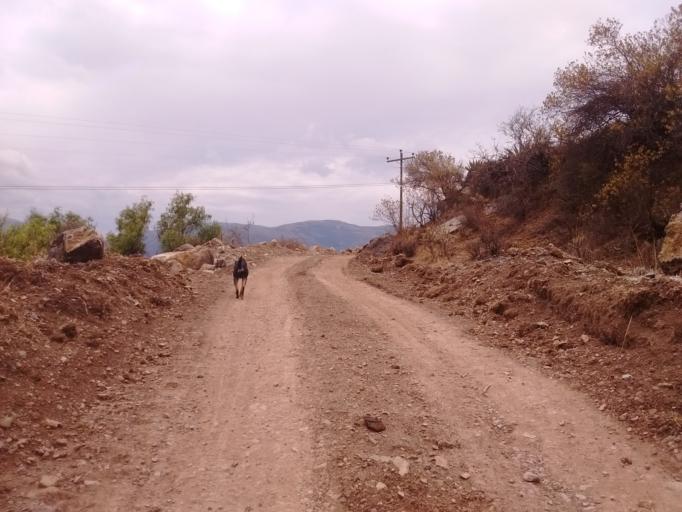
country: PE
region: Ayacucho
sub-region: Provincia de Victor Fajardo
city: Canaria
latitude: -13.8798
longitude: -73.9369
